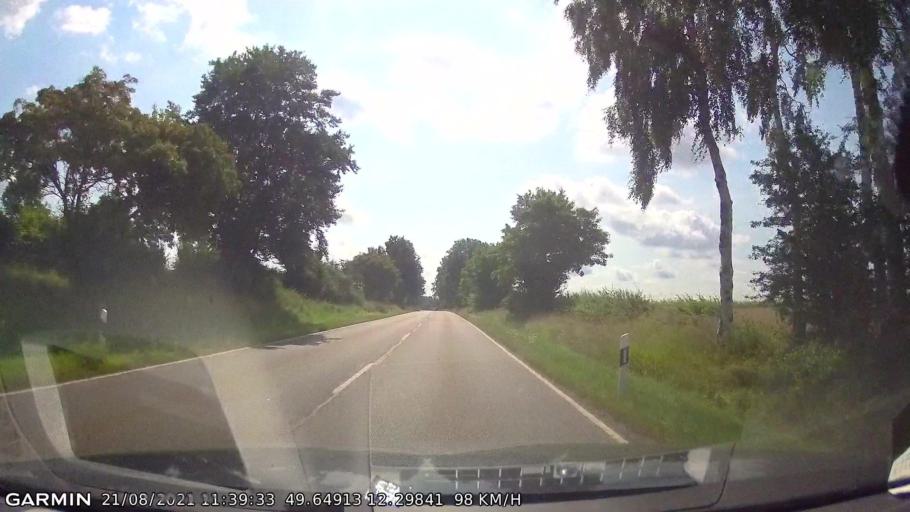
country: DE
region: Bavaria
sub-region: Upper Palatinate
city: Waldthurn
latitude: 49.6491
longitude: 12.2984
